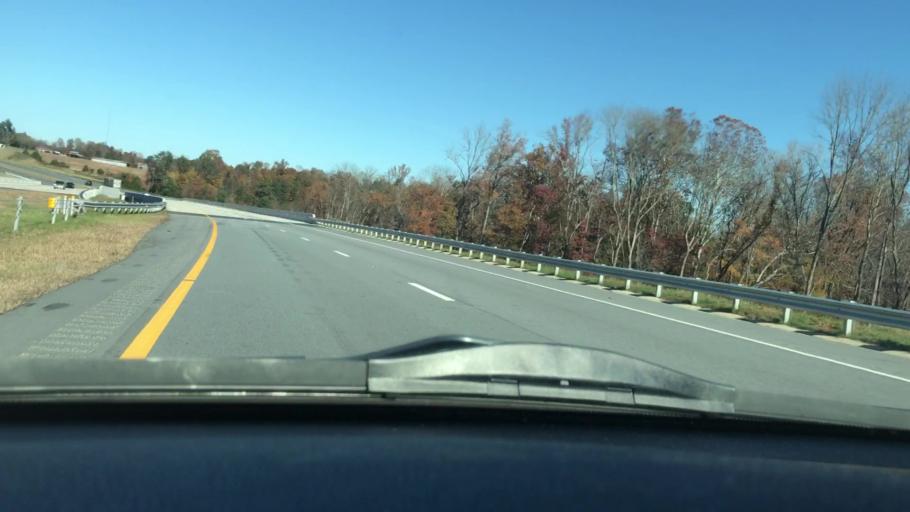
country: US
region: North Carolina
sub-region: Guilford County
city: Summerfield
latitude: 36.1765
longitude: -79.9355
